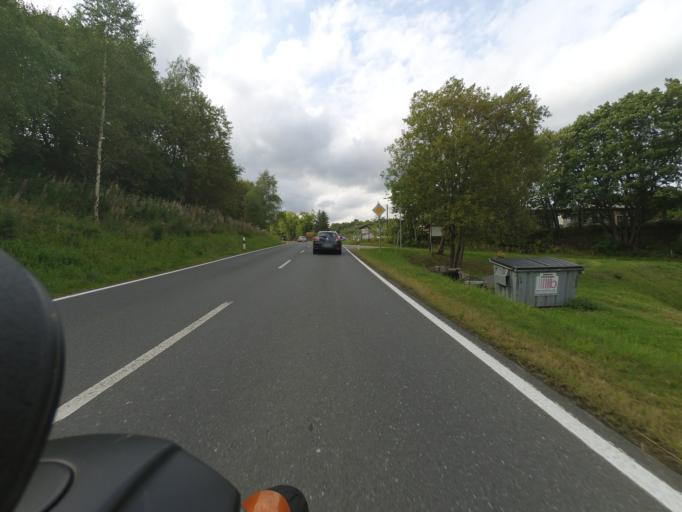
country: DE
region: Saxony
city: Altenberg
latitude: 50.7621
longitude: 13.7671
